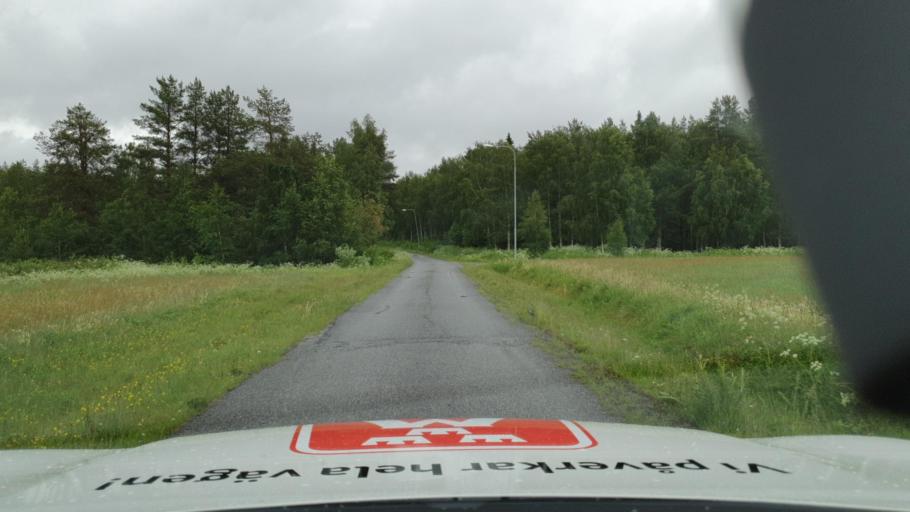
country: SE
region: Vaesterbotten
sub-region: Asele Kommun
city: Asele
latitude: 63.9397
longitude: 17.2744
